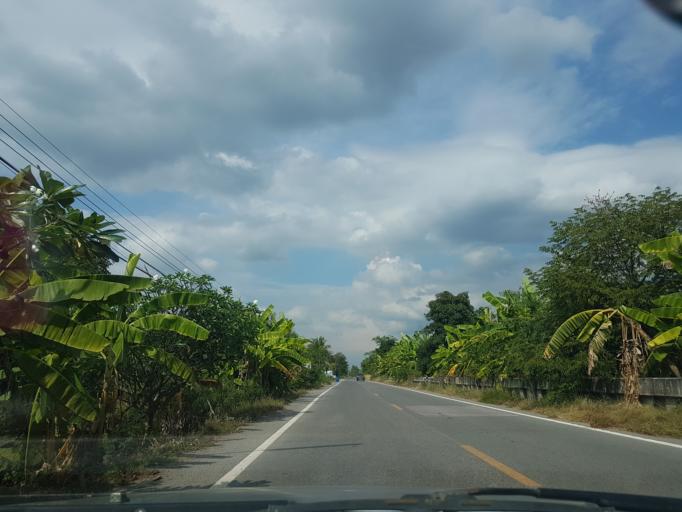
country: TH
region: Pathum Thani
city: Nong Suea
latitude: 14.1580
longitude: 100.8915
